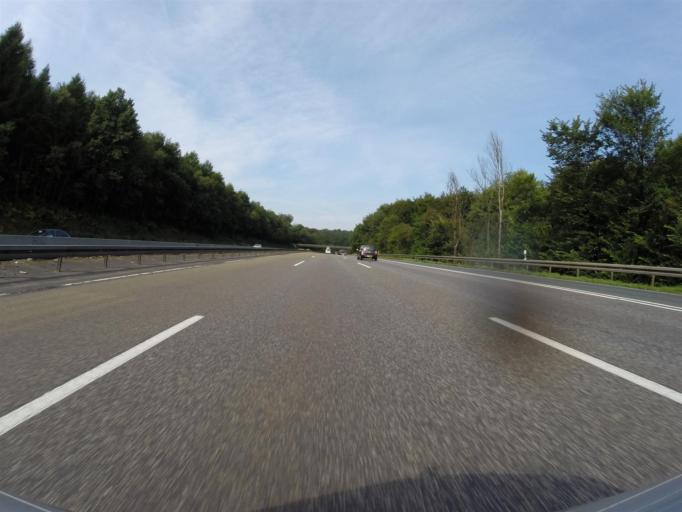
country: DE
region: Hesse
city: Schwarzenborn
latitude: 50.9525
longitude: 9.5085
